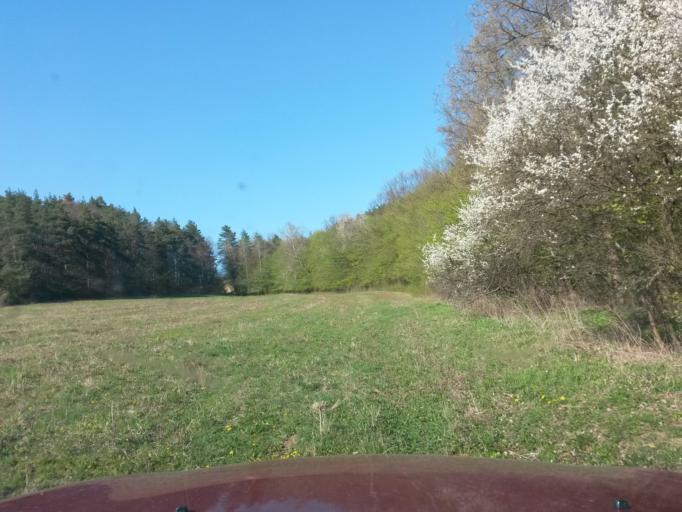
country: SK
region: Presovsky
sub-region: Okres Presov
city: Presov
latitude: 48.9619
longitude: 21.1106
